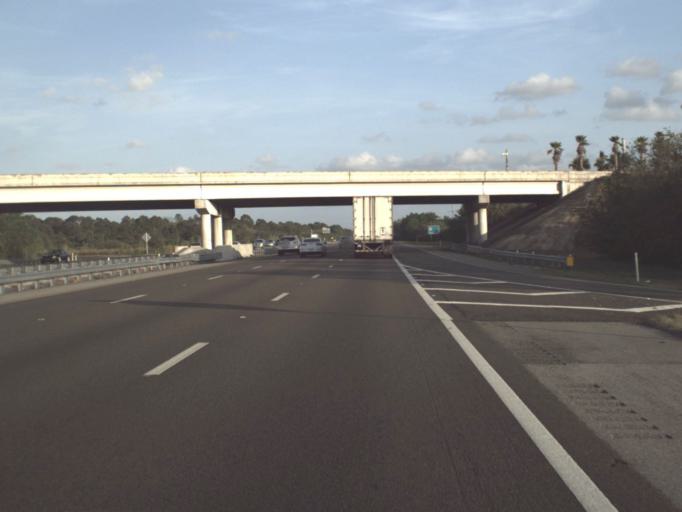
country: US
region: Florida
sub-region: Brevard County
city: Port Saint John
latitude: 28.5022
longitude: -80.8394
